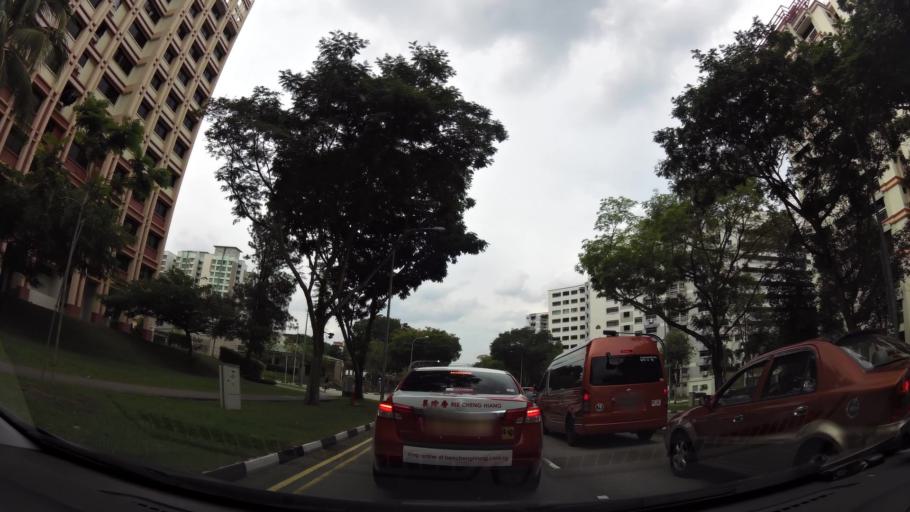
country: MY
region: Johor
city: Johor Bahru
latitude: 1.4364
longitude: 103.7958
